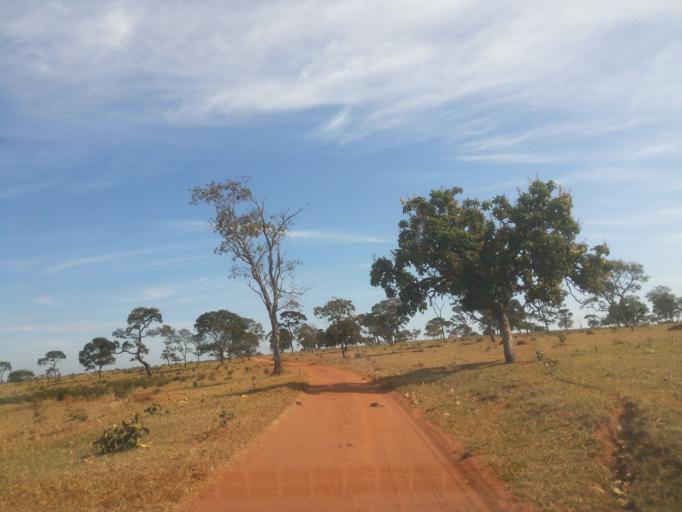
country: BR
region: Minas Gerais
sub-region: Ituiutaba
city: Ituiutaba
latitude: -19.1143
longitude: -49.4084
